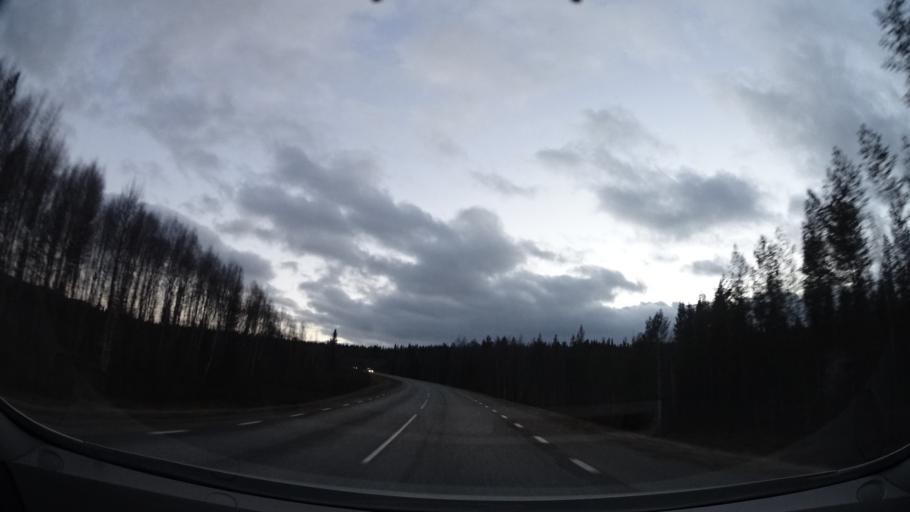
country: SE
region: Vaesterbotten
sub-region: Asele Kommun
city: Asele
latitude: 64.2092
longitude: 17.5122
